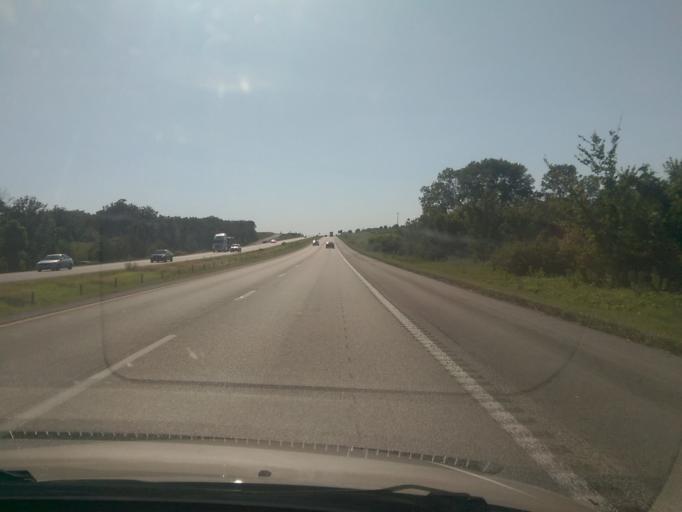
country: US
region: Missouri
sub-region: Saline County
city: Sweet Springs
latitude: 38.9733
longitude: -93.3186
